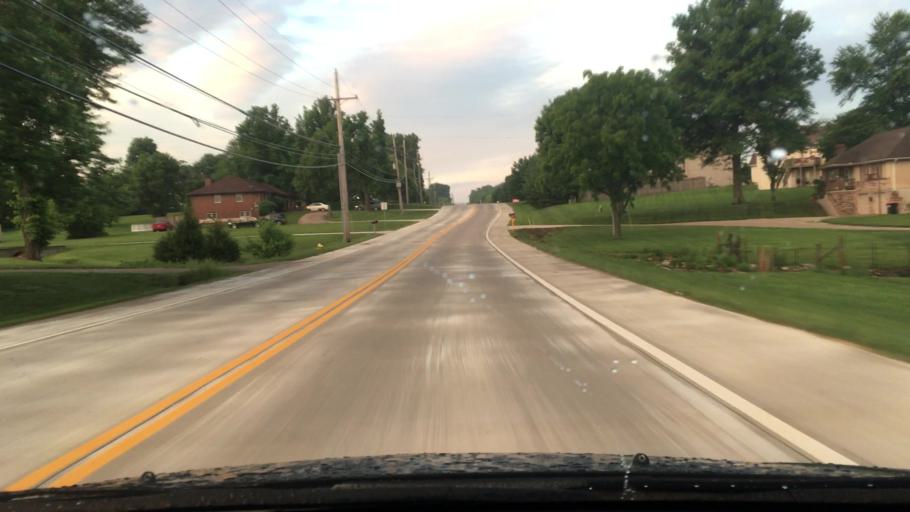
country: US
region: Missouri
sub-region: Jackson County
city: Lees Summit
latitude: 38.8646
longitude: -94.4166
